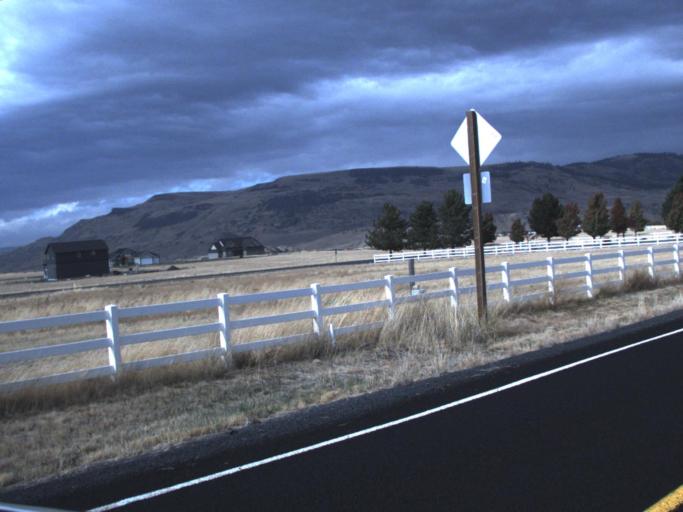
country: US
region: Washington
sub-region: Okanogan County
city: Coulee Dam
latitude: 47.9095
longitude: -118.6947
